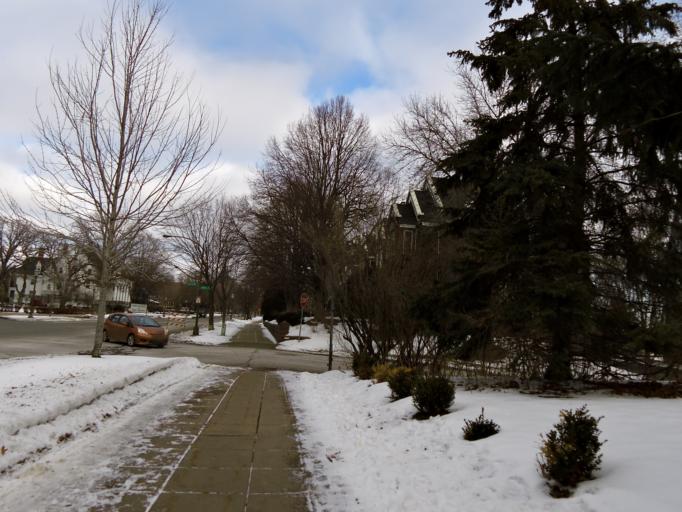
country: US
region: Minnesota
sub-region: Ramsey County
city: Saint Paul
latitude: 44.9421
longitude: -93.1163
